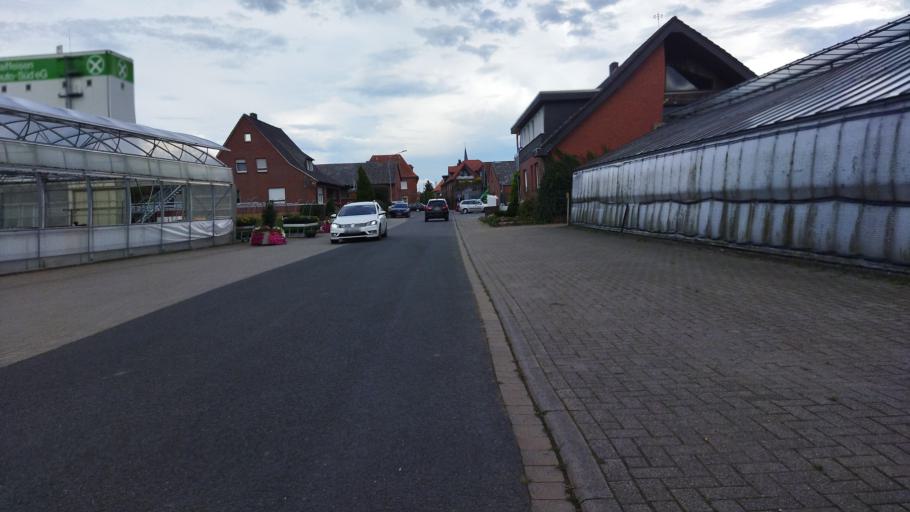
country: DE
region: Lower Saxony
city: Glandorf
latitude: 52.0801
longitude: 7.9947
